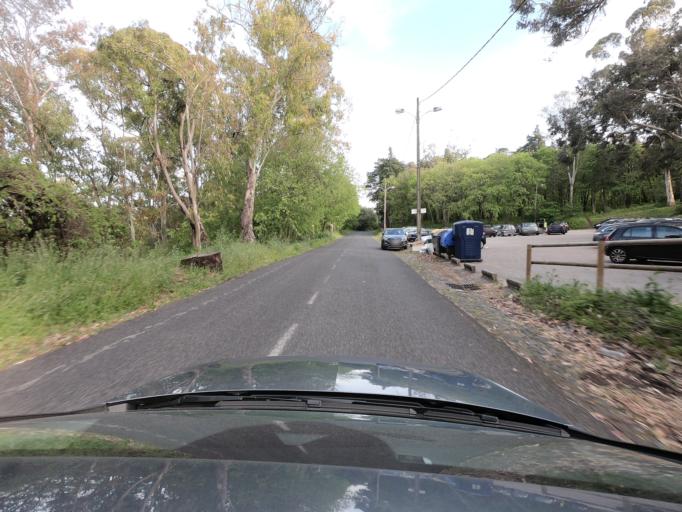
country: PT
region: Setubal
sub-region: Almada
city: Pragal
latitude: 38.7182
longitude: -9.1809
